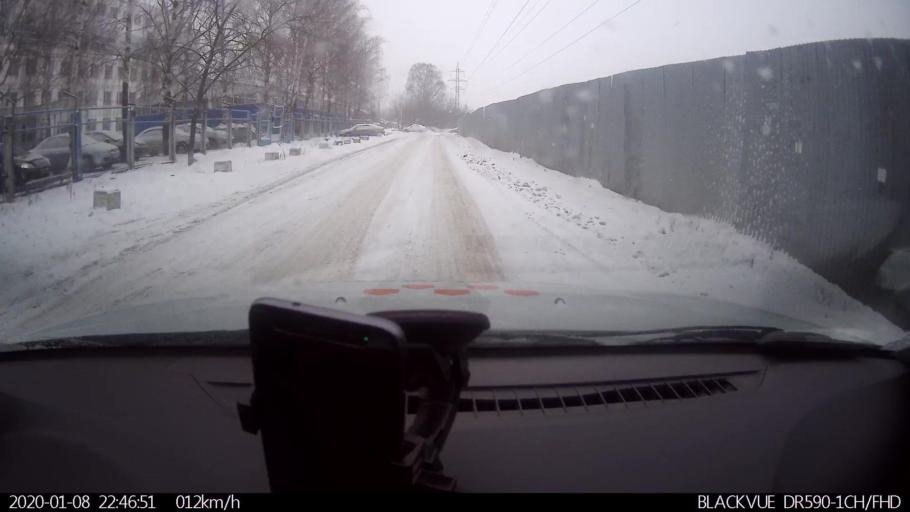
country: RU
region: Nizjnij Novgorod
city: Nizhniy Novgorod
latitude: 56.2941
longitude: 43.8927
